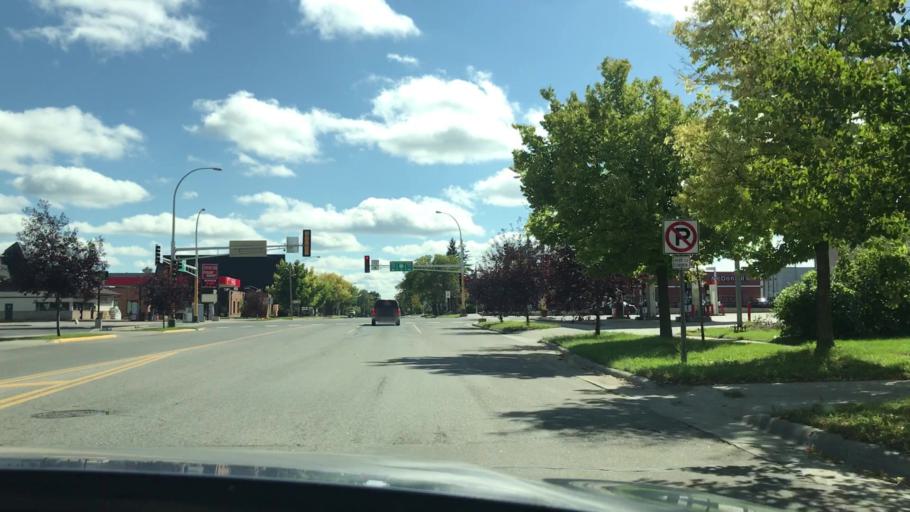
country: US
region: Minnesota
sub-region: Hubbard County
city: Park Rapids
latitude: 46.9229
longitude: -95.0586
